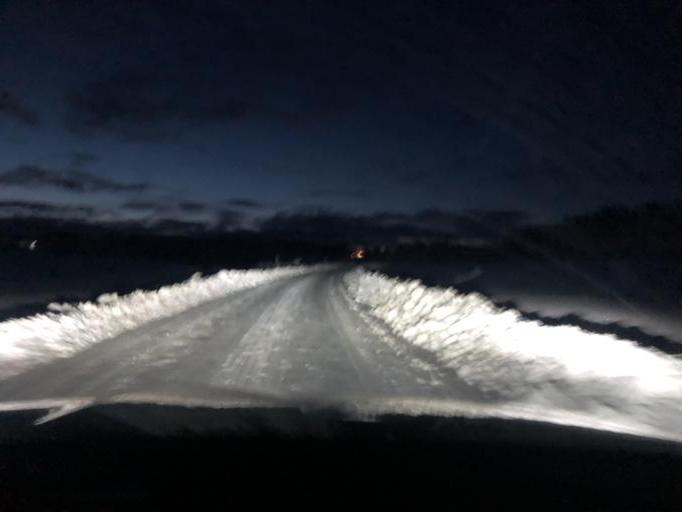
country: SE
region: Vaesternorrland
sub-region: Kramfors Kommun
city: Bollstabruk
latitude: 63.0541
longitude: 17.6585
